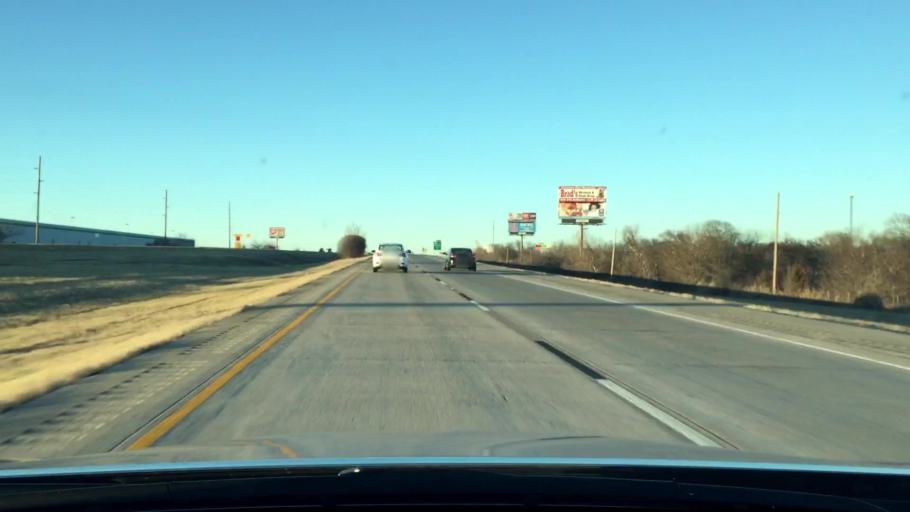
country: US
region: Oklahoma
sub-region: Love County
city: Marietta
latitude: 33.9318
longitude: -97.1346
